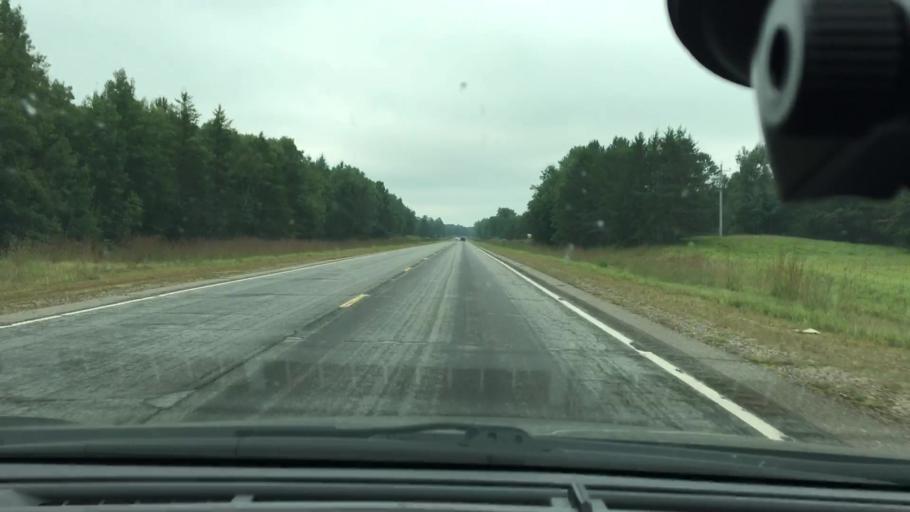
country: US
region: Minnesota
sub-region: Crow Wing County
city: Cross Lake
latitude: 46.6840
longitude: -93.9535
